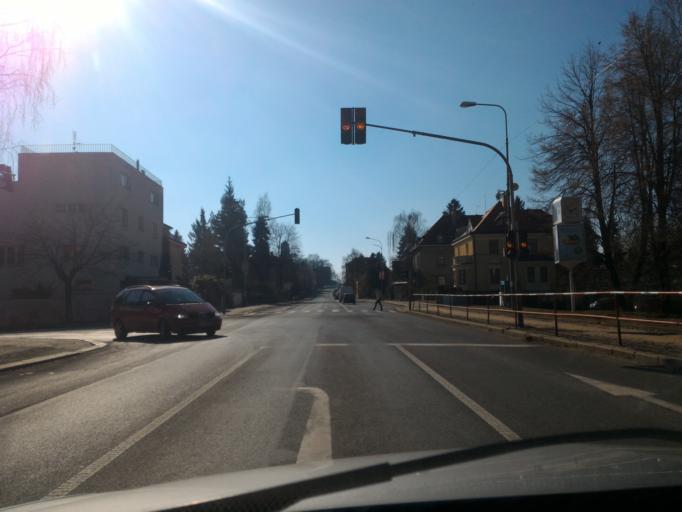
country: CZ
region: Liberecky
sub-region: Okres Jablonec nad Nisou
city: Jablonec nad Nisou
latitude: 50.7318
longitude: 15.1694
